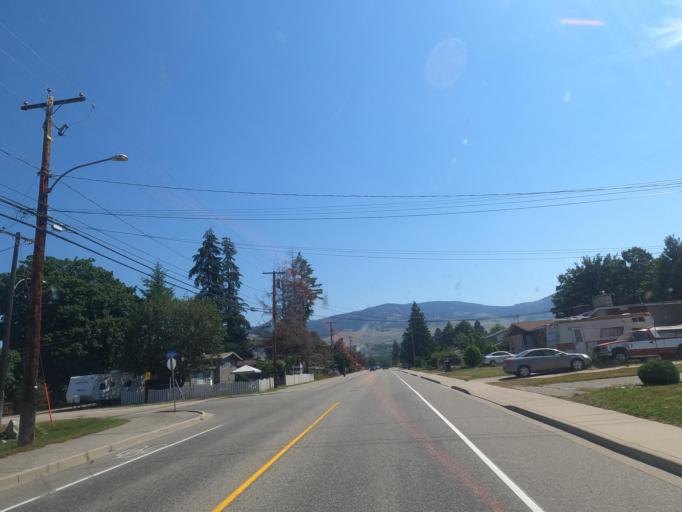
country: CA
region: British Columbia
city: Kelowna
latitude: 49.9011
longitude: -119.3925
